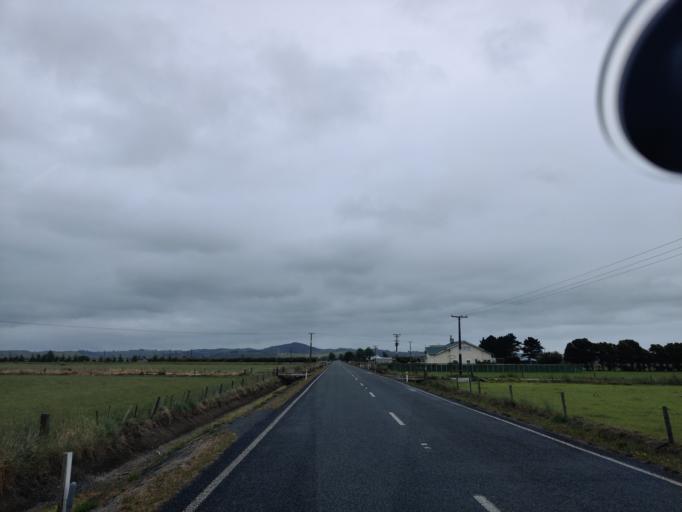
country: NZ
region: Northland
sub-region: Kaipara District
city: Dargaville
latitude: -36.1243
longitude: 174.0478
